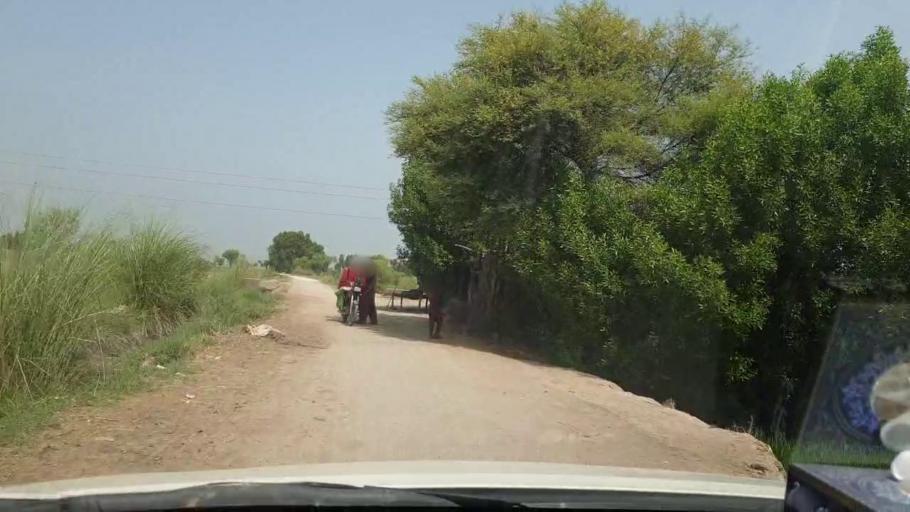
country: PK
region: Sindh
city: Shikarpur
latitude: 27.9883
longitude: 68.6978
